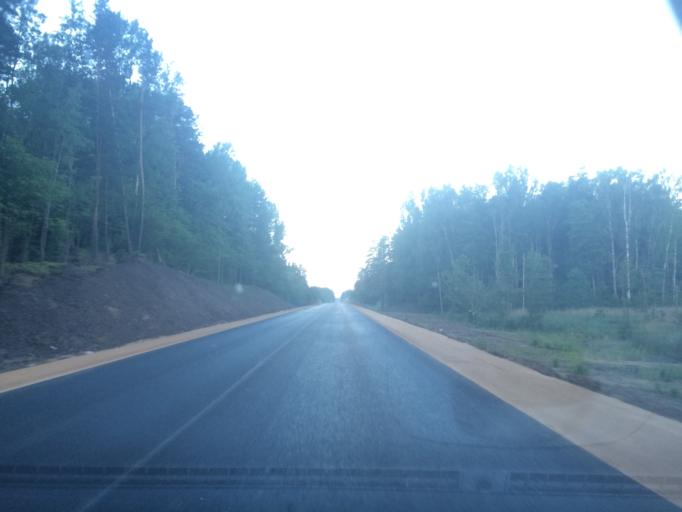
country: LT
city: Zarasai
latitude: 55.7664
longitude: 26.3396
